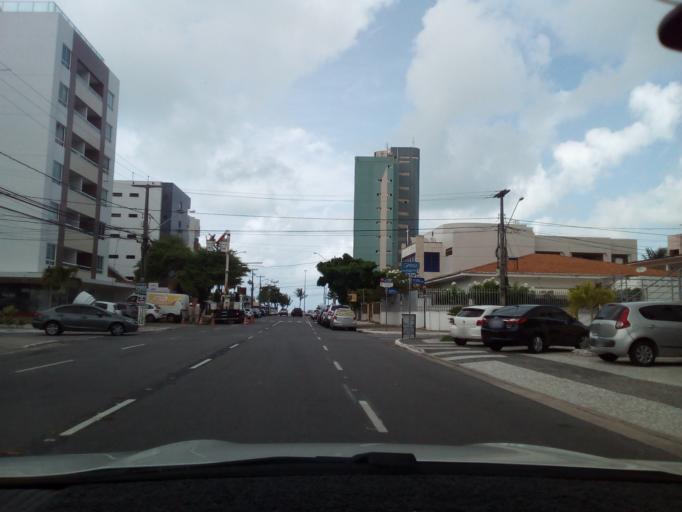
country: BR
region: Paraiba
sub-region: Joao Pessoa
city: Joao Pessoa
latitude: -7.1249
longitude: -34.8256
